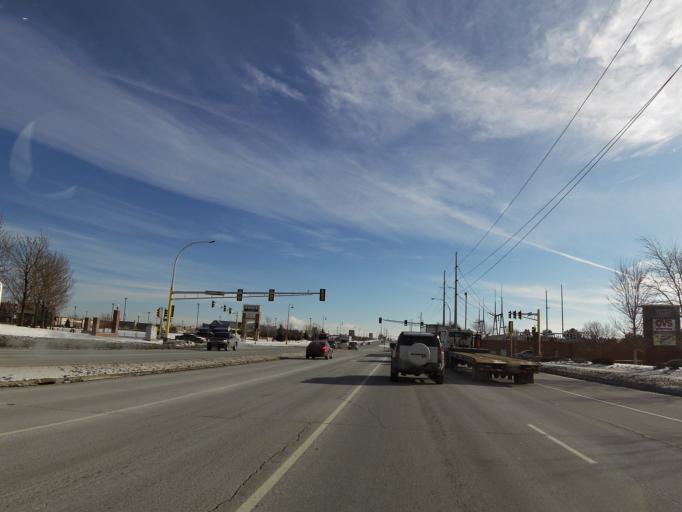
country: US
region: Minnesota
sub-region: Dakota County
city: Apple Valley
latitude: 44.7318
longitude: -93.2085
